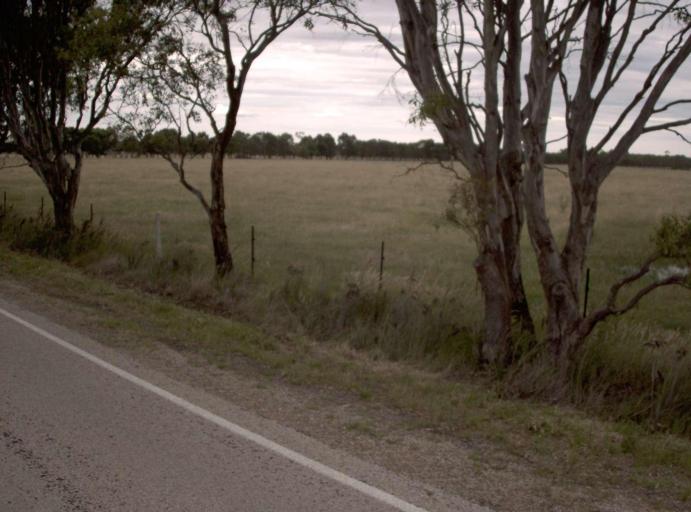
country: AU
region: Victoria
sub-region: East Gippsland
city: Bairnsdale
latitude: -37.9293
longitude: 147.5396
